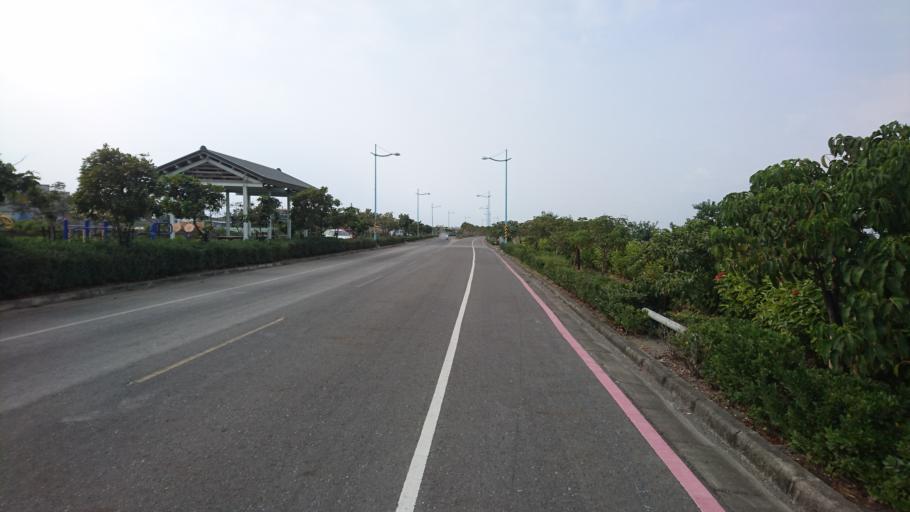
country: TW
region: Taiwan
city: Fengshan
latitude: 22.4341
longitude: 120.4815
